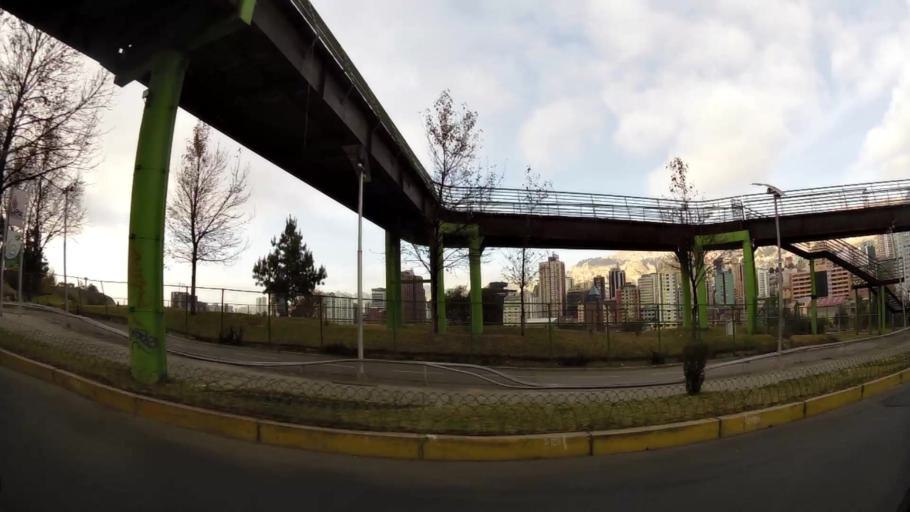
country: BO
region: La Paz
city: La Paz
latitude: -16.5025
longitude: -68.1257
